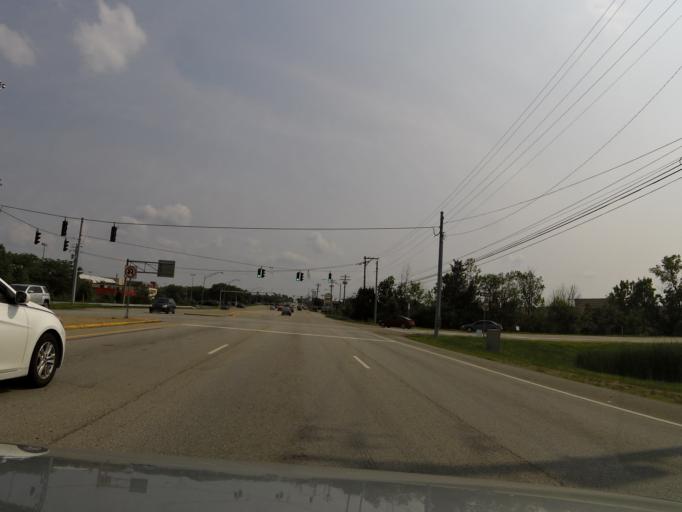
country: US
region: Ohio
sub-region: Hamilton County
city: Springdale
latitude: 39.2937
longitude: -84.4665
